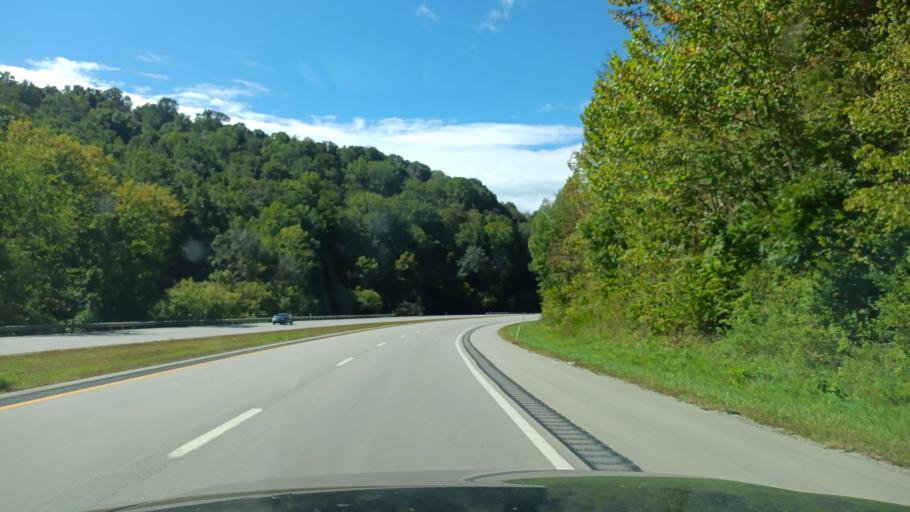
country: US
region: West Virginia
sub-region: Harrison County
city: Salem
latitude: 39.2837
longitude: -80.6618
